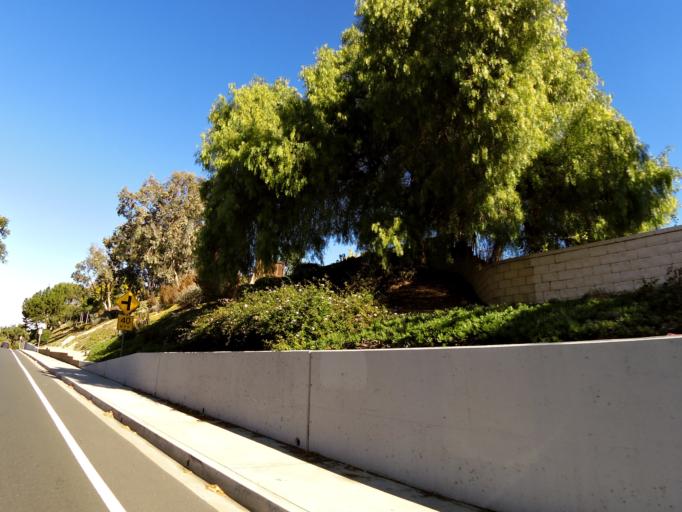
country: US
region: California
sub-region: Ventura County
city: Thousand Oaks
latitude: 34.1893
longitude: -118.8744
